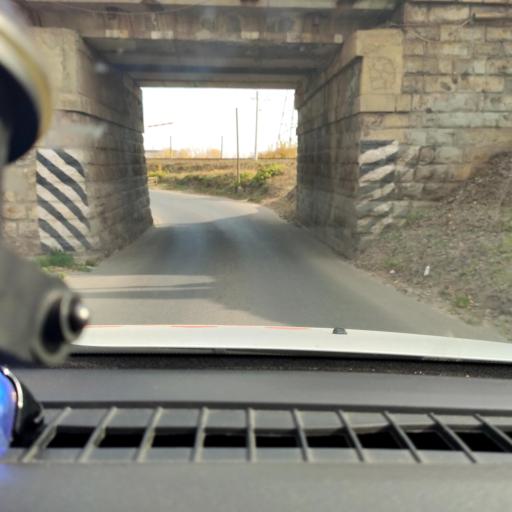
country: RU
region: Samara
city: Samara
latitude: 53.1809
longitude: 50.1057
